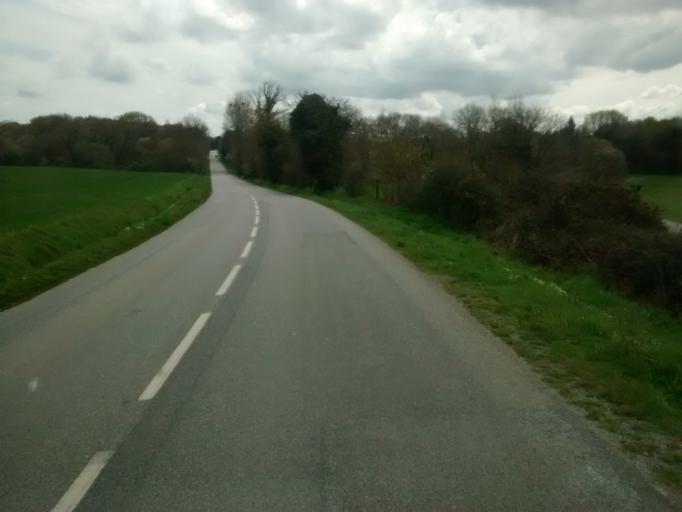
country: FR
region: Brittany
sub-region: Departement du Morbihan
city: Ploermel
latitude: 47.9053
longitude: -2.3797
